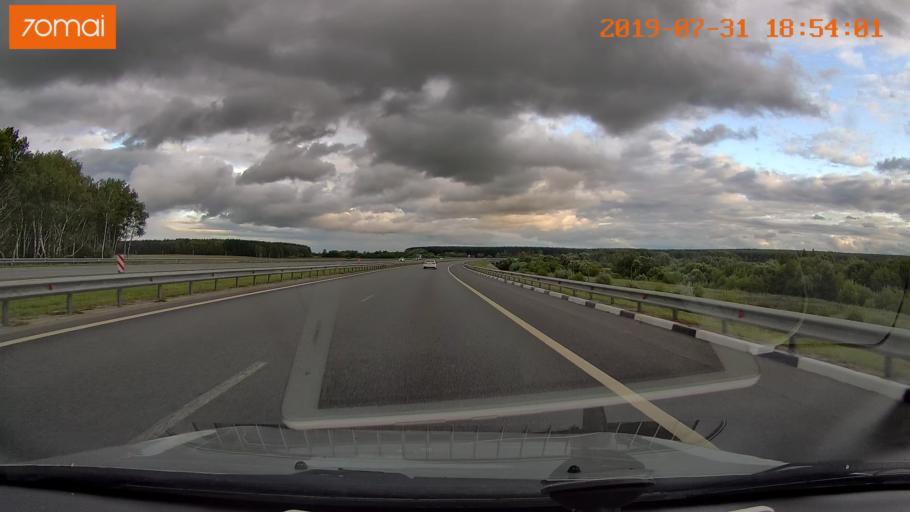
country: RU
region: Moskovskaya
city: Raduzhnyy
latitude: 55.1951
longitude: 38.6655
